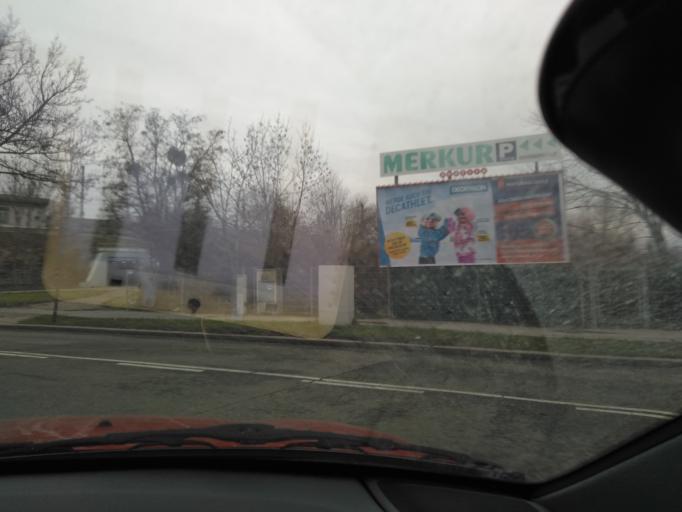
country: AT
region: Lower Austria
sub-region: Politischer Bezirk Modling
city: Vosendorf
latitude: 48.1589
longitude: 16.3351
